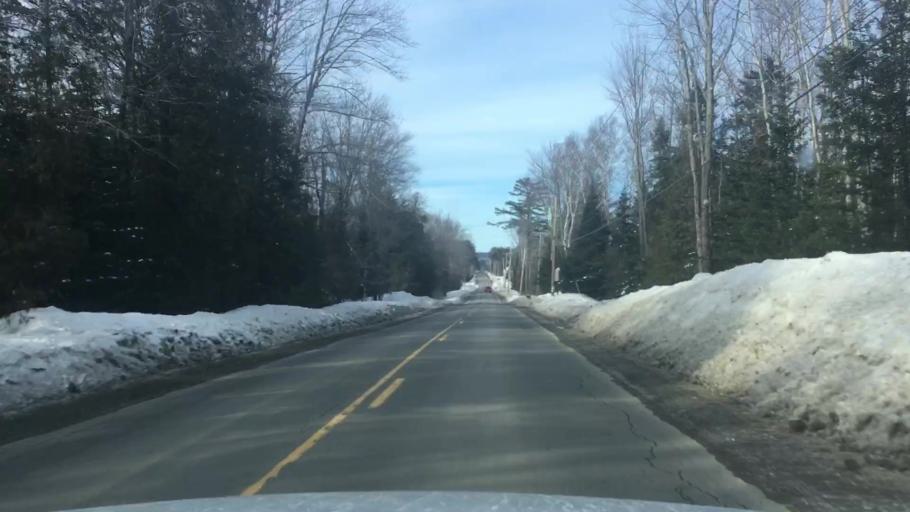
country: US
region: Maine
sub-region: Penobscot County
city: Charleston
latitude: 45.0480
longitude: -69.0293
